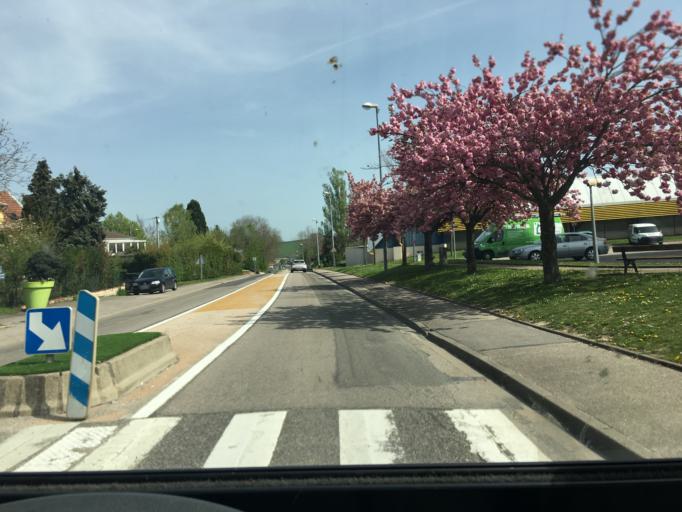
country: FR
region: Lorraine
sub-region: Departement de Meurthe-et-Moselle
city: Saint-Nicolas-de-Port
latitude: 48.6251
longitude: 6.2933
